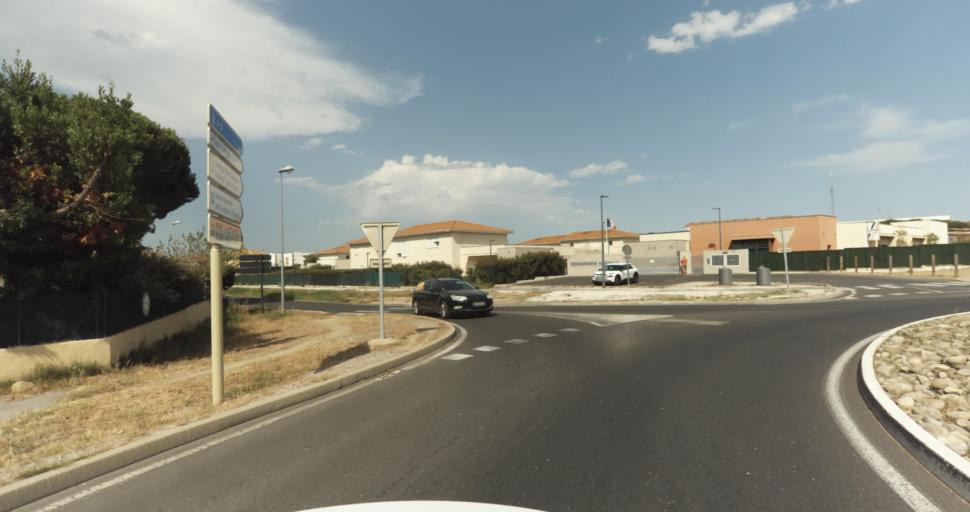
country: FR
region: Languedoc-Roussillon
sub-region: Departement des Pyrenees-Orientales
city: Elne
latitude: 42.6035
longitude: 2.9732
